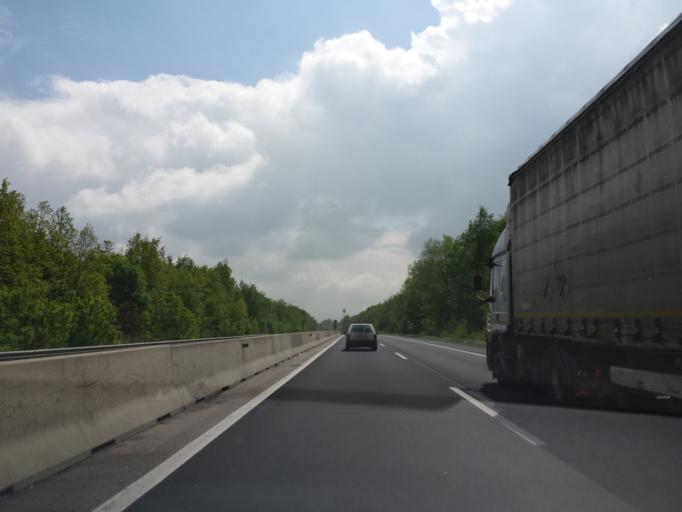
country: AT
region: Lower Austria
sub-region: Politischer Bezirk Bruck an der Leitha
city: Trautmannsdorf an der Leitha
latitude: 48.0630
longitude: 16.6992
